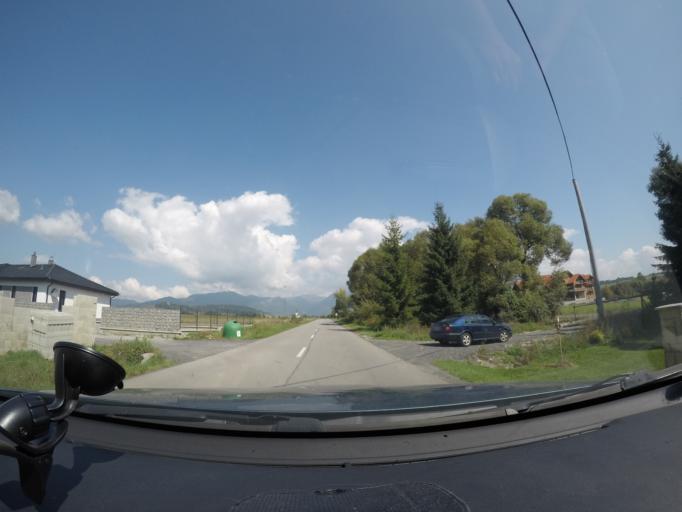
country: SK
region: Zilinsky
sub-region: Okres Liptovsky Mikulas
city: Liptovsky Mikulas
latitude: 49.1066
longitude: 19.5988
